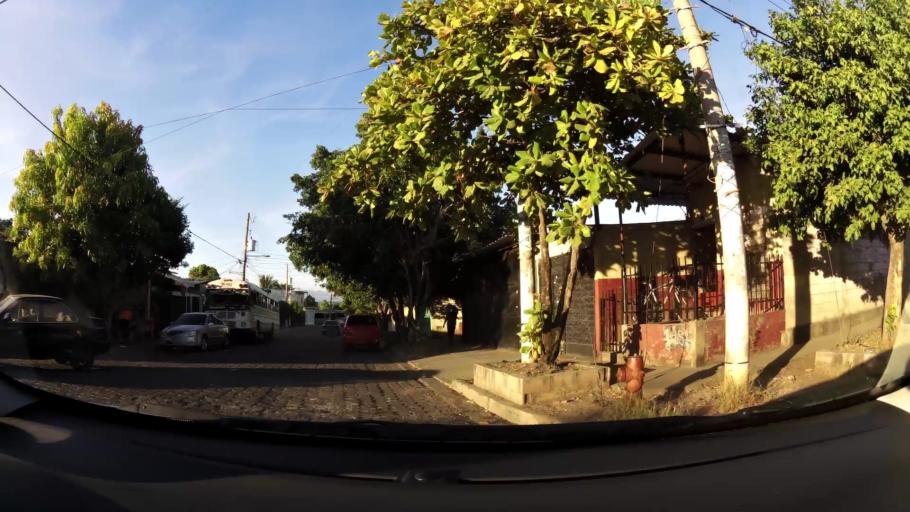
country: SV
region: San Miguel
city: San Miguel
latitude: 13.4690
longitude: -88.1635
